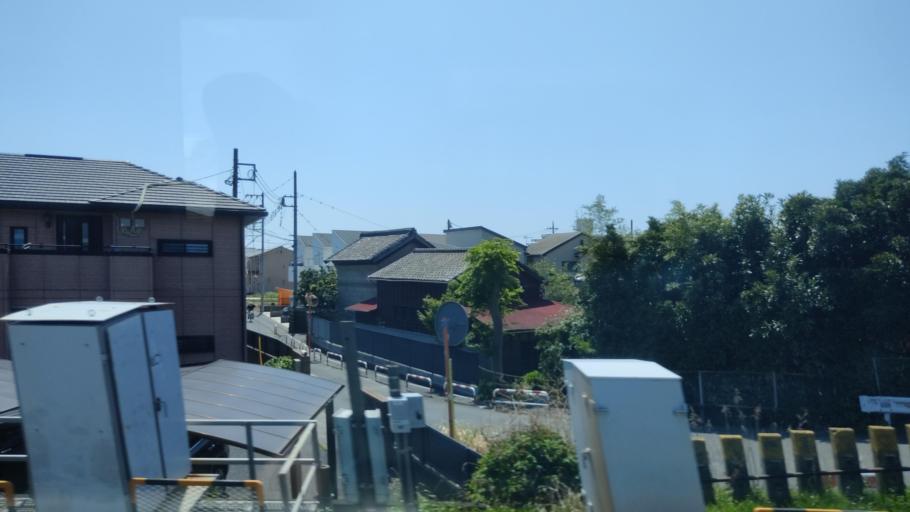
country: JP
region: Kanagawa
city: Chigasaki
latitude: 35.3288
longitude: 139.3846
